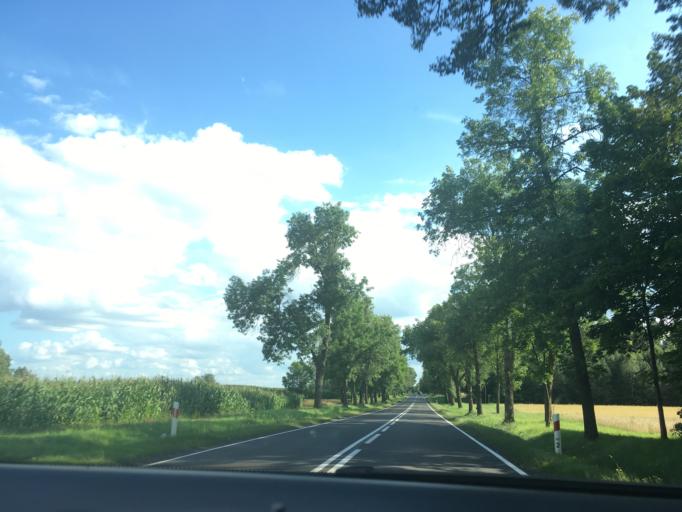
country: PL
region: Podlasie
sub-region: Powiat bielski
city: Bielsk Podlaski
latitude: 52.8519
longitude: 23.1971
